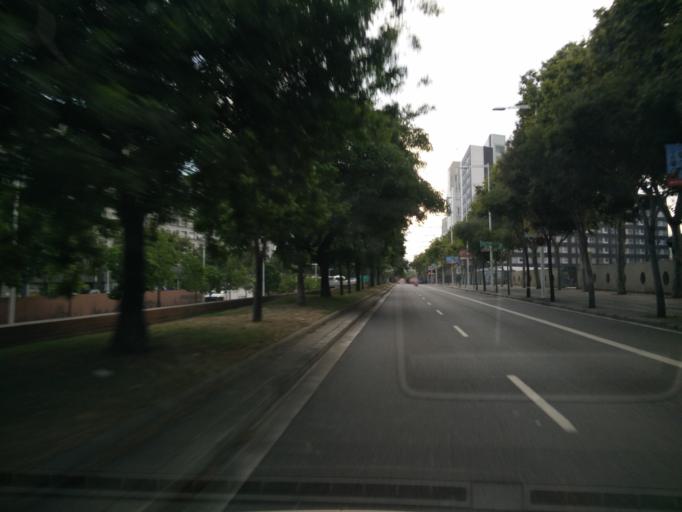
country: ES
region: Catalonia
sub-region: Provincia de Barcelona
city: Ciutat Vella
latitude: 41.3835
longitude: 2.1888
